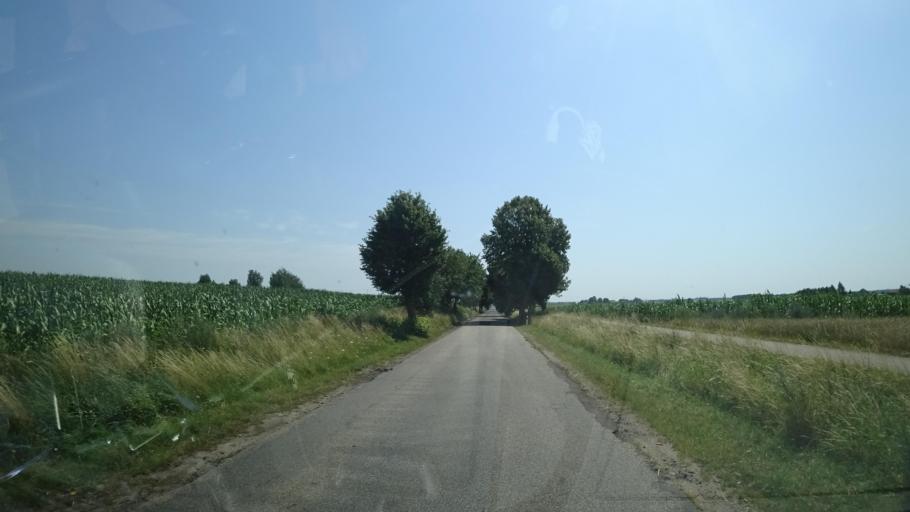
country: PL
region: Pomeranian Voivodeship
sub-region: Powiat chojnicki
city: Brusy
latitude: 53.8772
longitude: 17.6536
